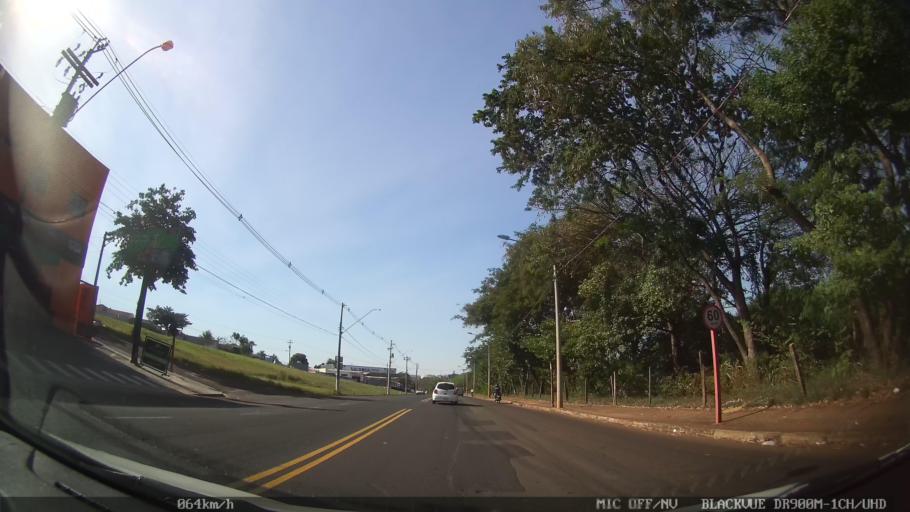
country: BR
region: Sao Paulo
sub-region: Sao Jose Do Rio Preto
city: Sao Jose do Rio Preto
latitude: -20.7851
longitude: -49.3843
